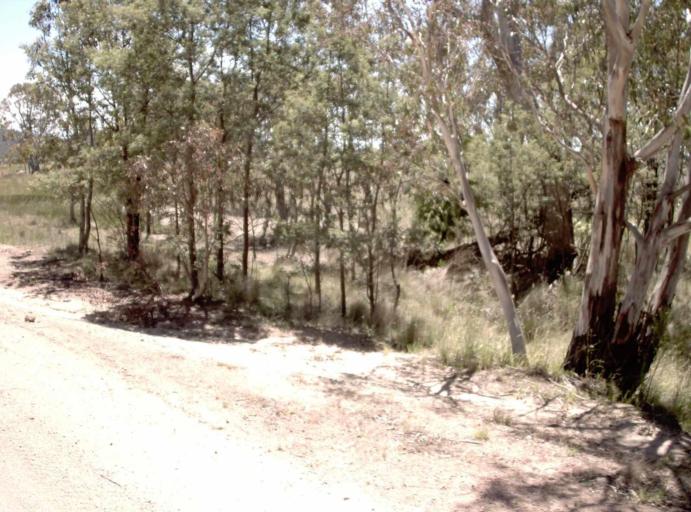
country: AU
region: New South Wales
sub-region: Snowy River
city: Jindabyne
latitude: -37.0239
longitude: 148.2738
